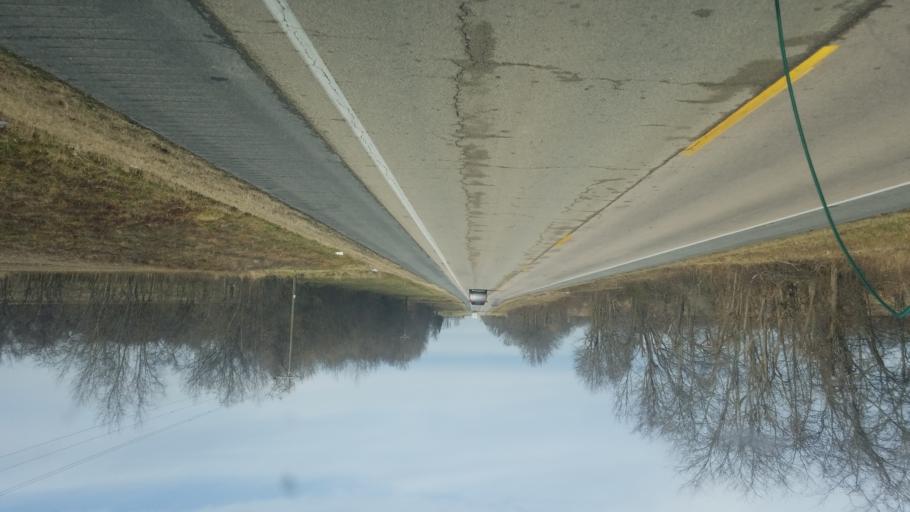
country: US
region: Missouri
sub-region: Stoddard County
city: Advance
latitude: 37.0083
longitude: -89.9046
